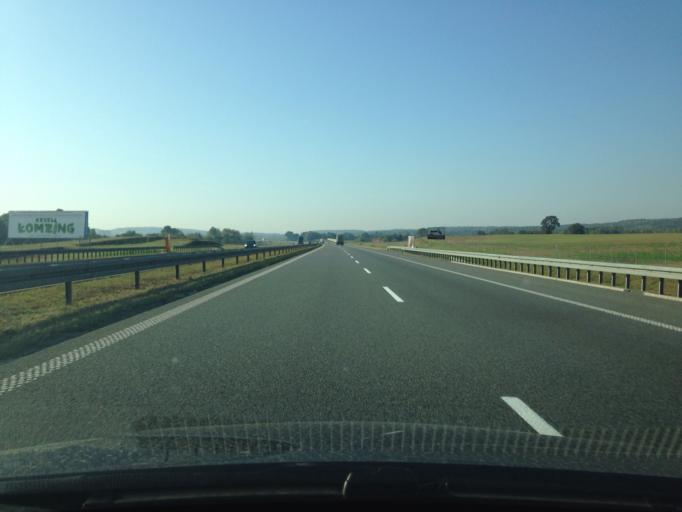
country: PL
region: Pomeranian Voivodeship
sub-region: Powiat tczewski
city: Pelplin
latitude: 53.9572
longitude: 18.6513
